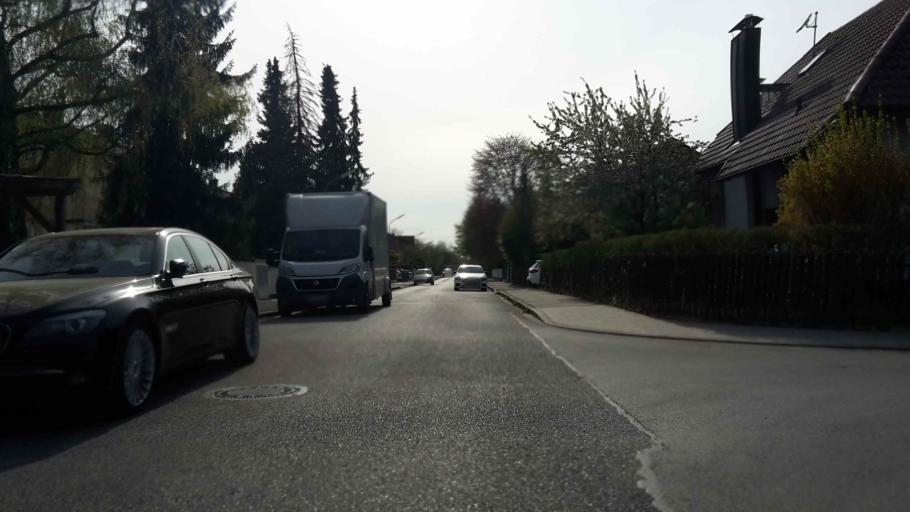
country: DE
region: Bavaria
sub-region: Upper Bavaria
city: Karlsfeld
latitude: 48.1870
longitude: 11.4482
